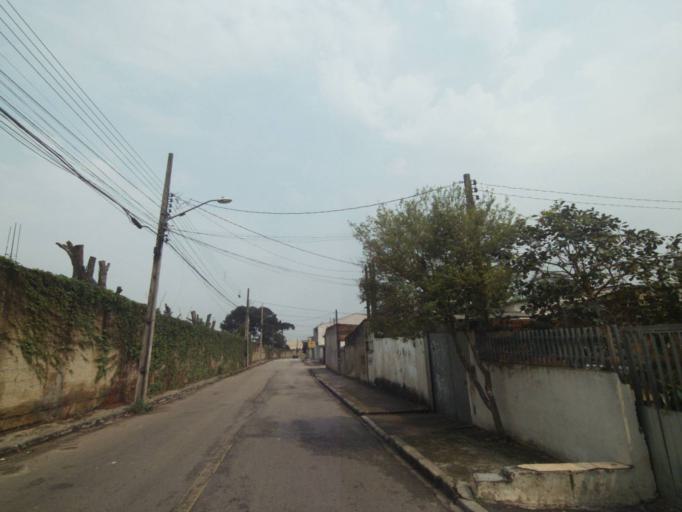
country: BR
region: Parana
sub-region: Curitiba
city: Curitiba
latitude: -25.4826
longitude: -49.2990
